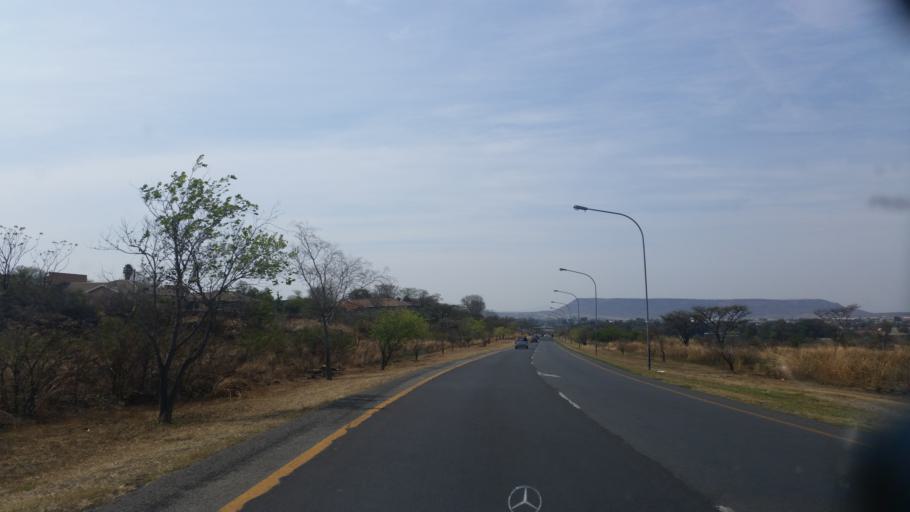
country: ZA
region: KwaZulu-Natal
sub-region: uThukela District Municipality
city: Ladysmith
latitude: -28.5660
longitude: 29.7598
